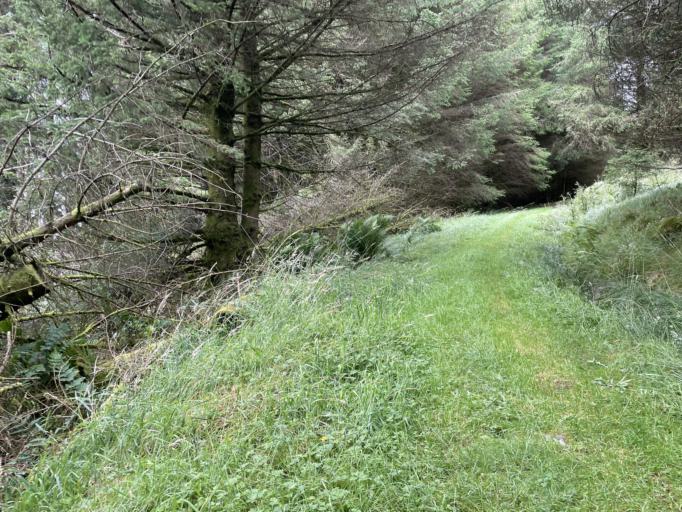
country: GB
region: Scotland
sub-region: South Ayrshire
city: Maybole
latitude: 55.1987
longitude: -4.6704
